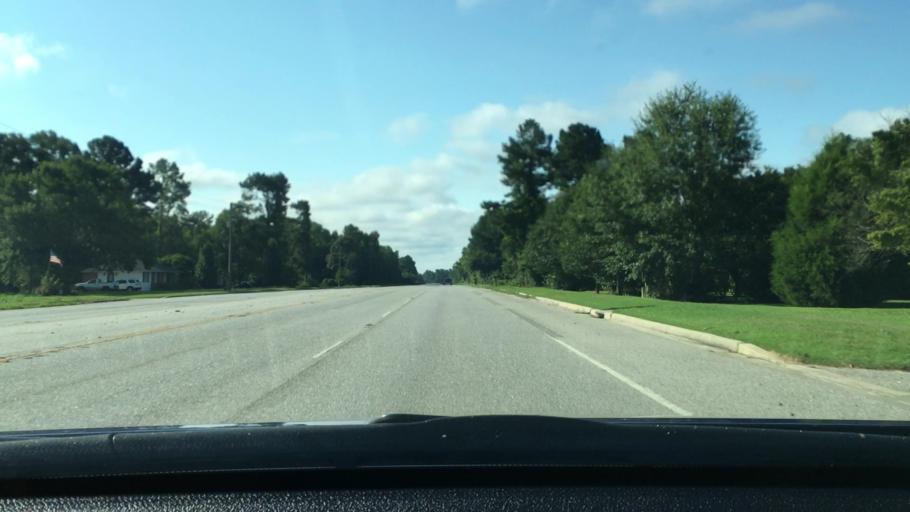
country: US
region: South Carolina
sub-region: Clarendon County
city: Manning
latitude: 33.7590
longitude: -80.2274
